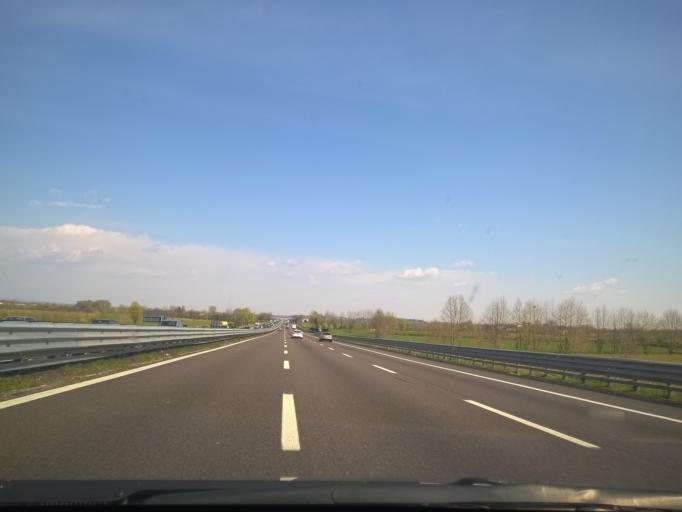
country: IT
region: Lombardy
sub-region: Provincia di Brescia
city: Desenzano del Garda
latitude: 45.4437
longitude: 10.5490
